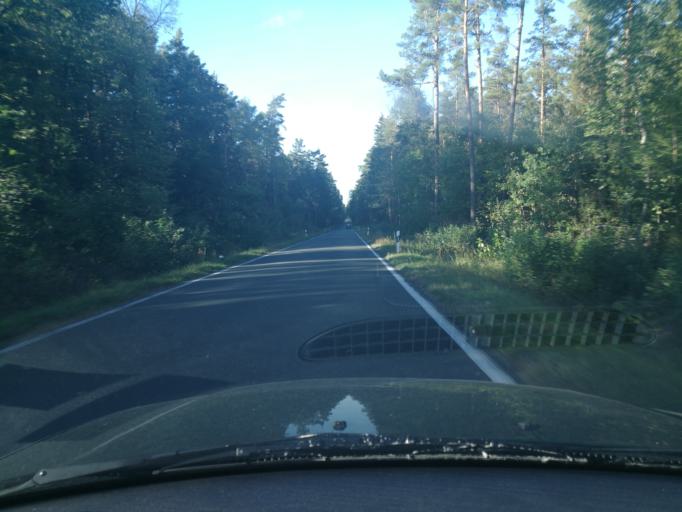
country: DE
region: Bavaria
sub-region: Regierungsbezirk Mittelfranken
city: Hessdorf
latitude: 49.6169
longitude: 10.9383
